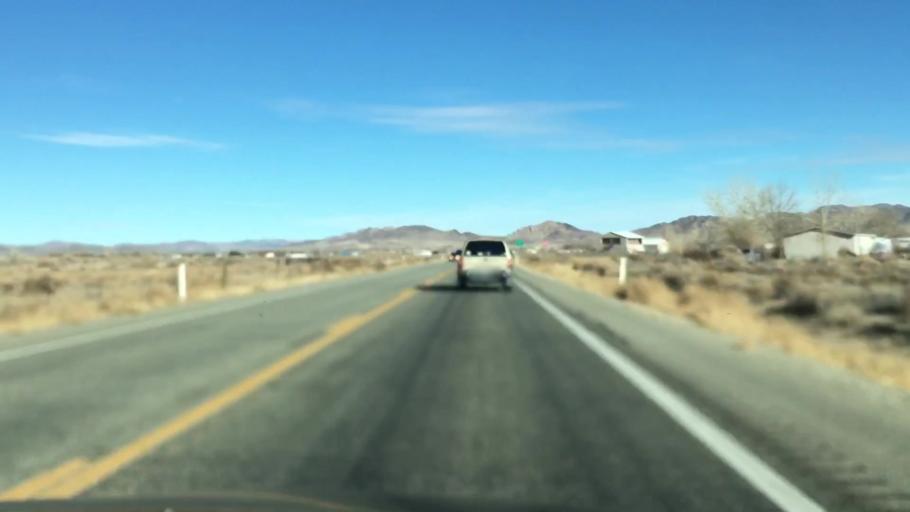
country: US
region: Nevada
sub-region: Lyon County
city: Yerington
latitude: 39.0043
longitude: -119.0896
